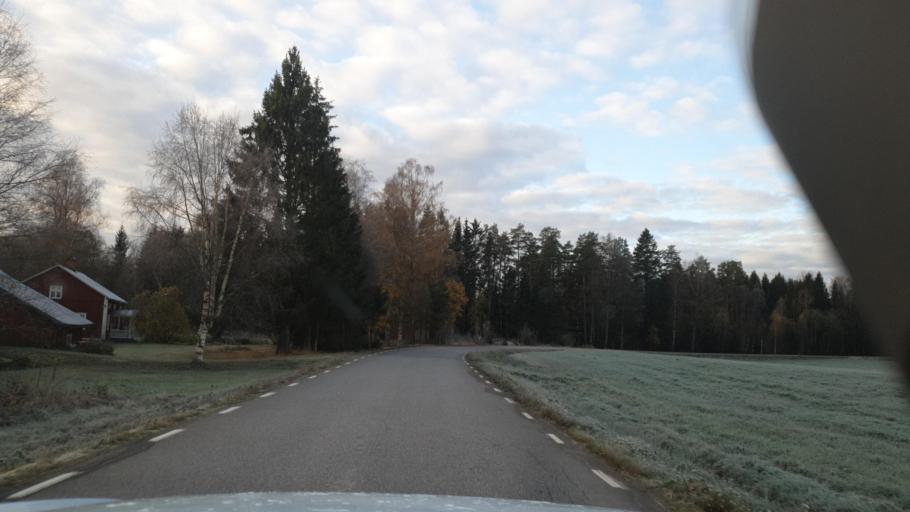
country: SE
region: Vaermland
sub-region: Eda Kommun
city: Amotfors
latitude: 59.7258
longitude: 12.1684
